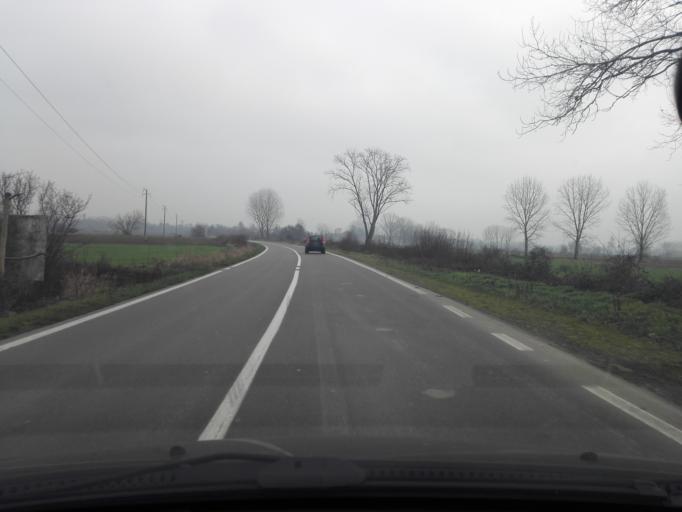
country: IT
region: Piedmont
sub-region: Provincia di Alessandria
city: Bosco Marengo
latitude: 44.8261
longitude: 8.6603
